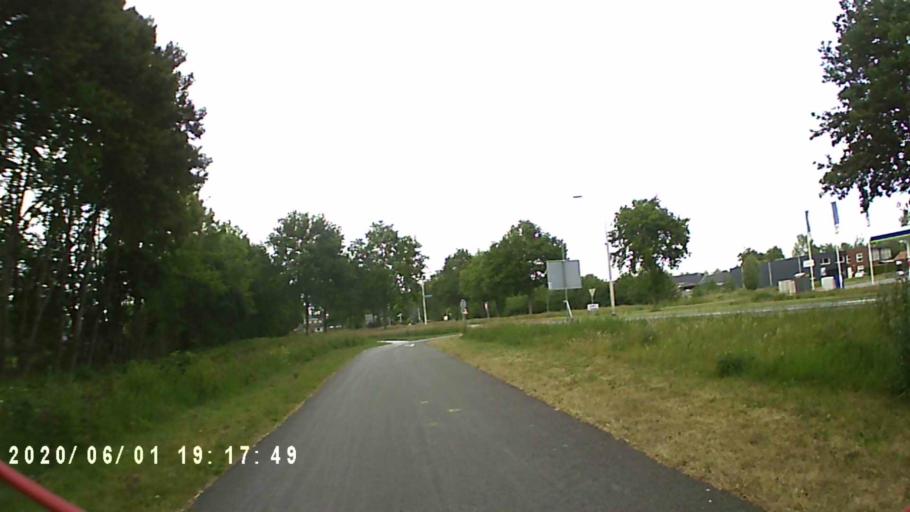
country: NL
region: Friesland
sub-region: Gemeente Achtkarspelen
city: Drogeham
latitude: 53.2033
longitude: 6.1037
